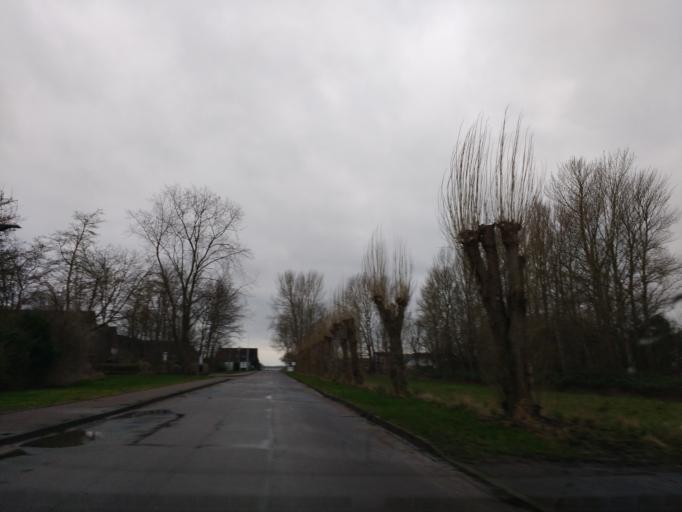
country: DE
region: Schleswig-Holstein
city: Grossenbrode
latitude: 54.3567
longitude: 11.0835
